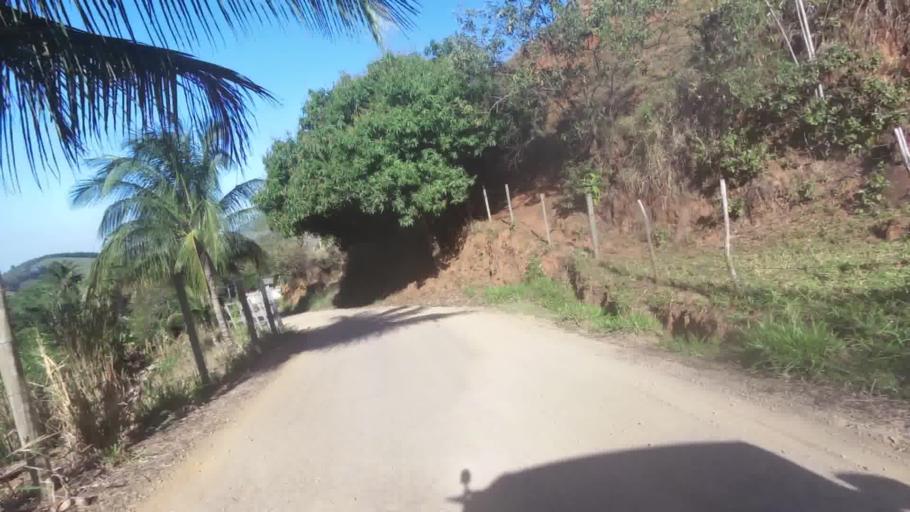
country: BR
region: Espirito Santo
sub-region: Iconha
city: Iconha
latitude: -20.7403
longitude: -40.7934
